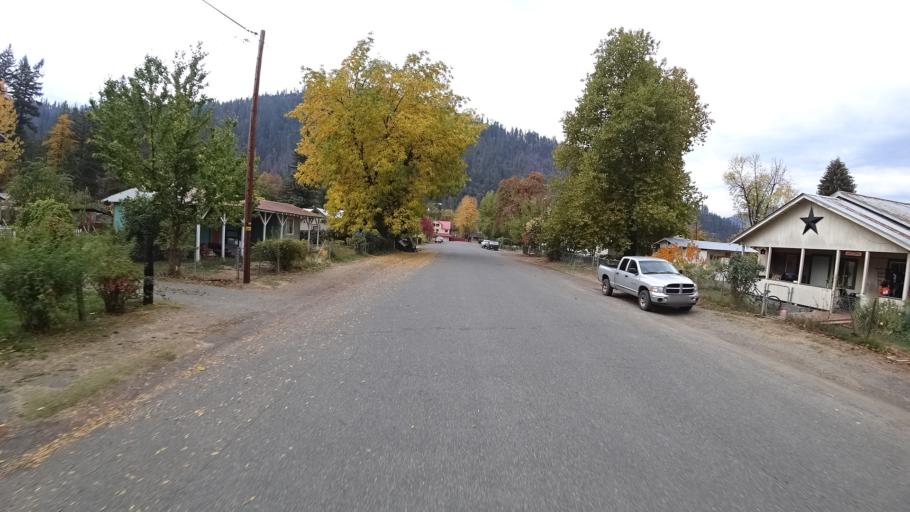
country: US
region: California
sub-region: Siskiyou County
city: Happy Camp
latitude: 41.7942
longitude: -123.3776
